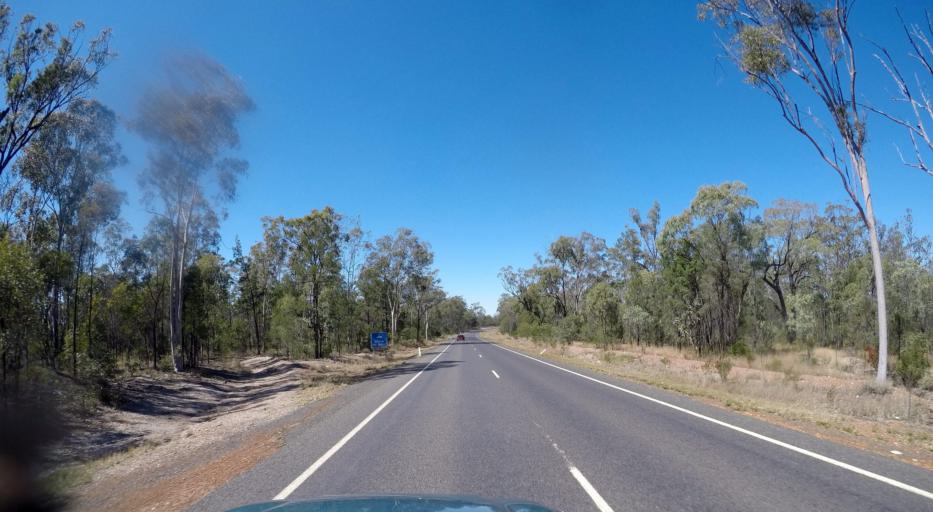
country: AU
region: Queensland
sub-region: Western Downs
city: Westcourt
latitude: -26.4816
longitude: 150.0774
